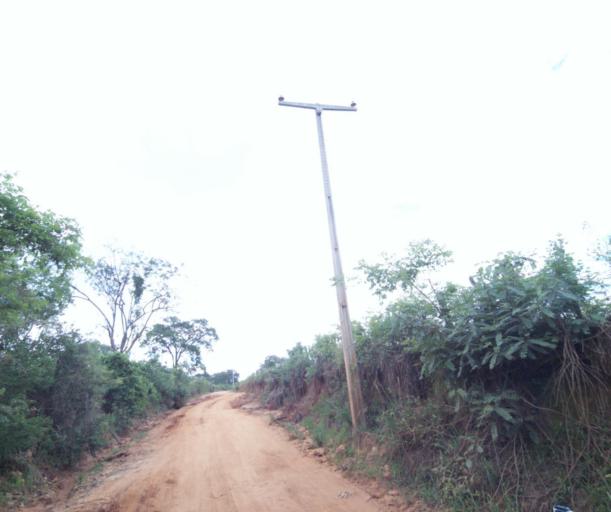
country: BR
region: Bahia
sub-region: Carinhanha
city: Carinhanha
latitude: -14.1865
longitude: -44.4952
